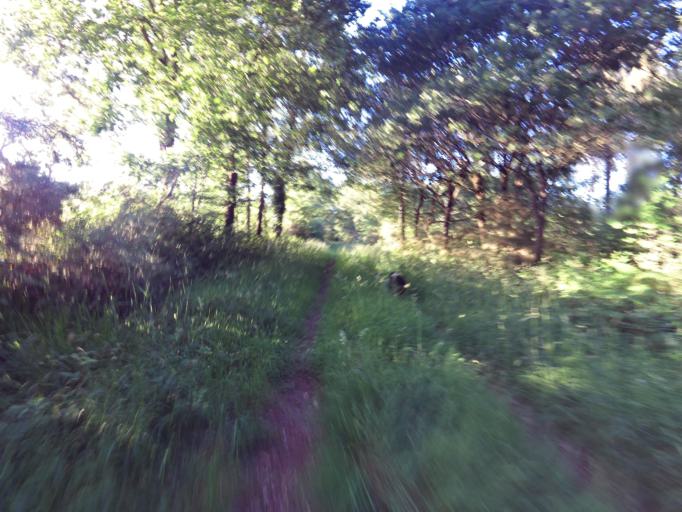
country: FR
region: Brittany
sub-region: Departement du Morbihan
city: Molac
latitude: 47.7517
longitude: -2.4133
